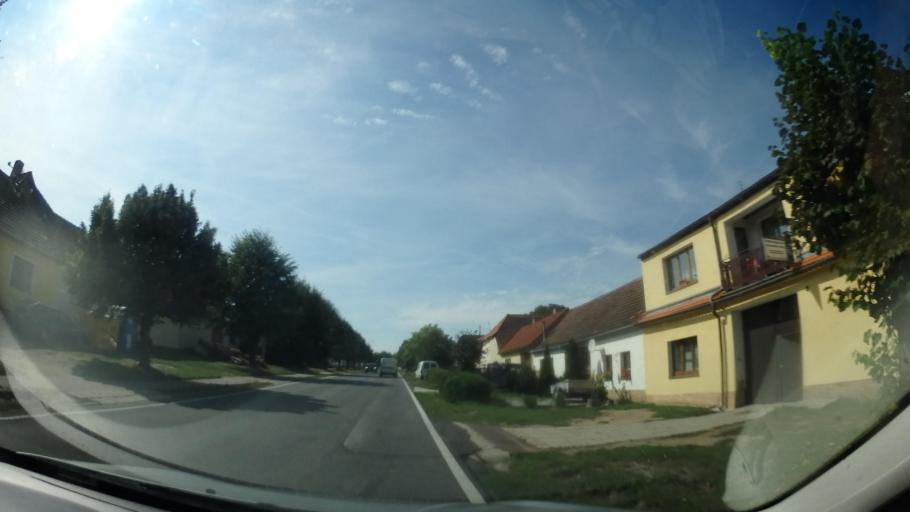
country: CZ
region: Jihocesky
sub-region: Okres Pisek
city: Pisek
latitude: 49.2949
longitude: 14.0424
